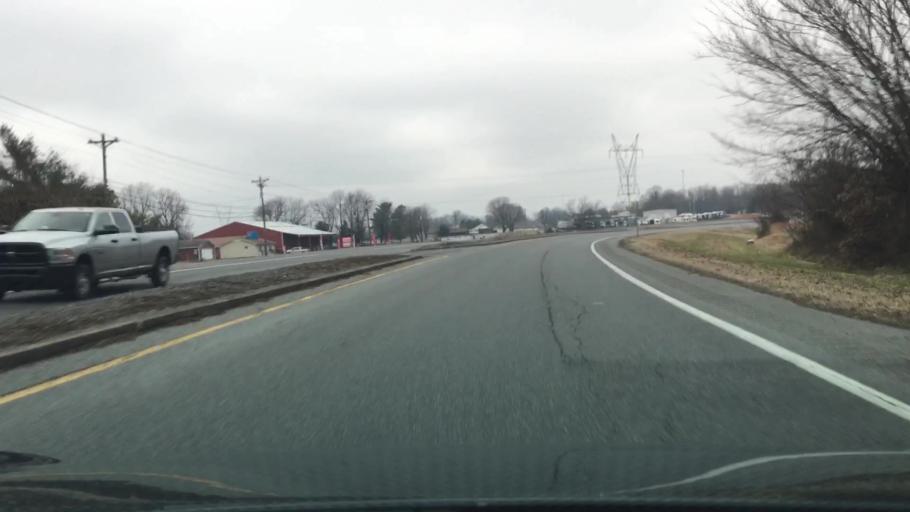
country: US
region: Kentucky
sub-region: McCracken County
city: Reidland
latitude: 36.9880
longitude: -88.5032
